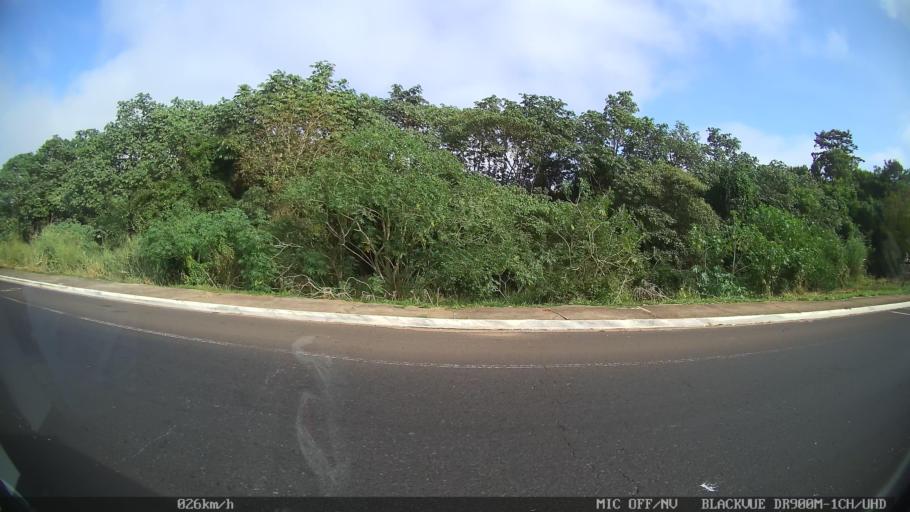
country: BR
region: Sao Paulo
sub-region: Sao Jose Do Rio Preto
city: Sao Jose do Rio Preto
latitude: -20.8153
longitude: -49.4341
